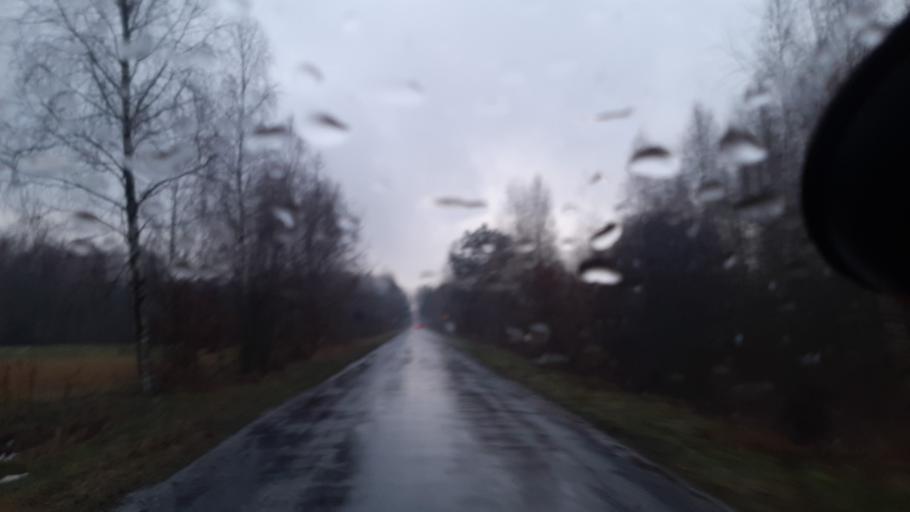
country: PL
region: Lublin Voivodeship
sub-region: Powiat lubartowski
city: Firlej
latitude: 51.5280
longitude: 22.5018
